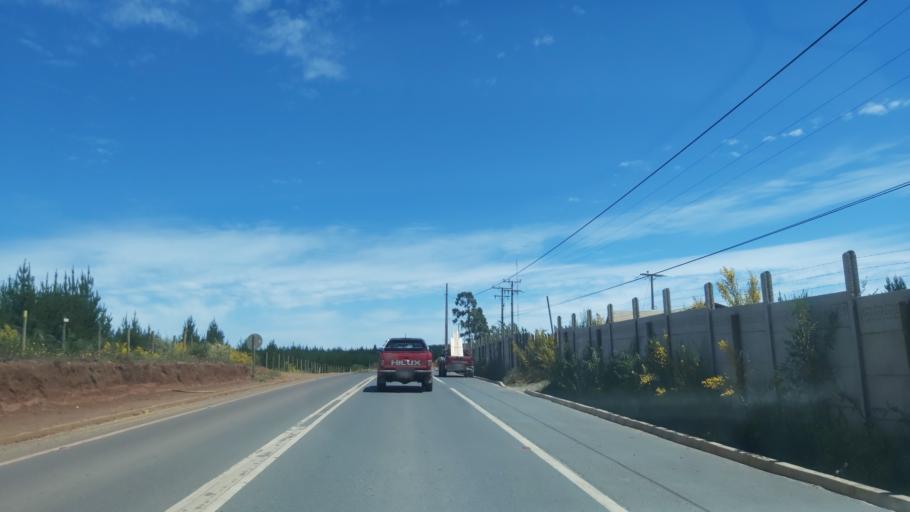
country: CL
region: Maule
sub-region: Provincia de Talca
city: Constitucion
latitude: -35.4023
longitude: -72.4369
